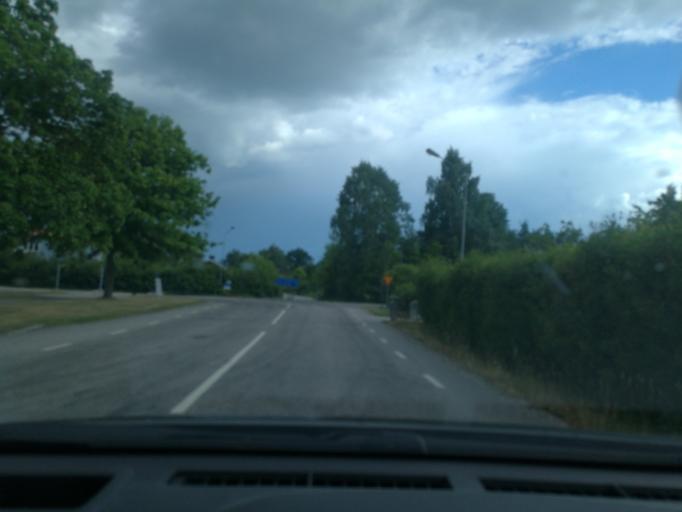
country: SE
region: Soedermanland
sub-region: Eskilstuna Kommun
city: Arla
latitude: 59.3831
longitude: 16.6761
